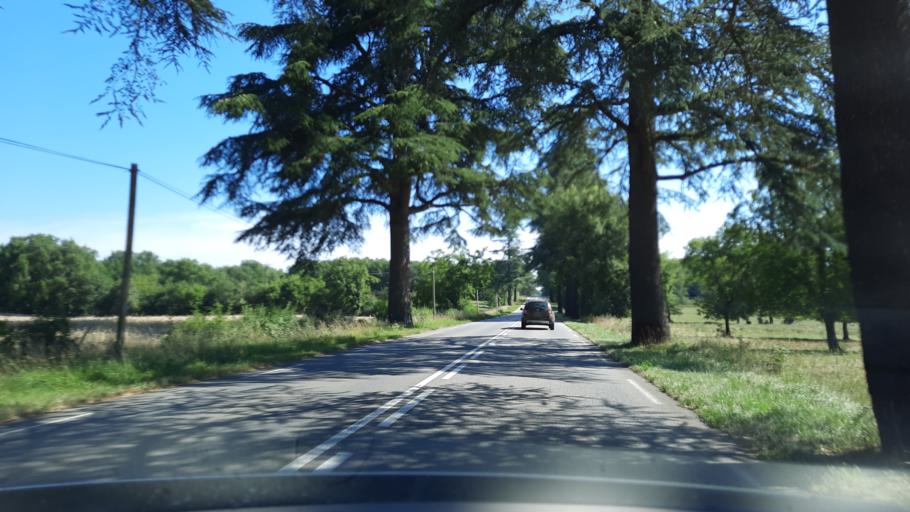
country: FR
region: Midi-Pyrenees
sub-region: Departement du Tarn-et-Garonne
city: Caylus
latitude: 44.3014
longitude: 1.8769
